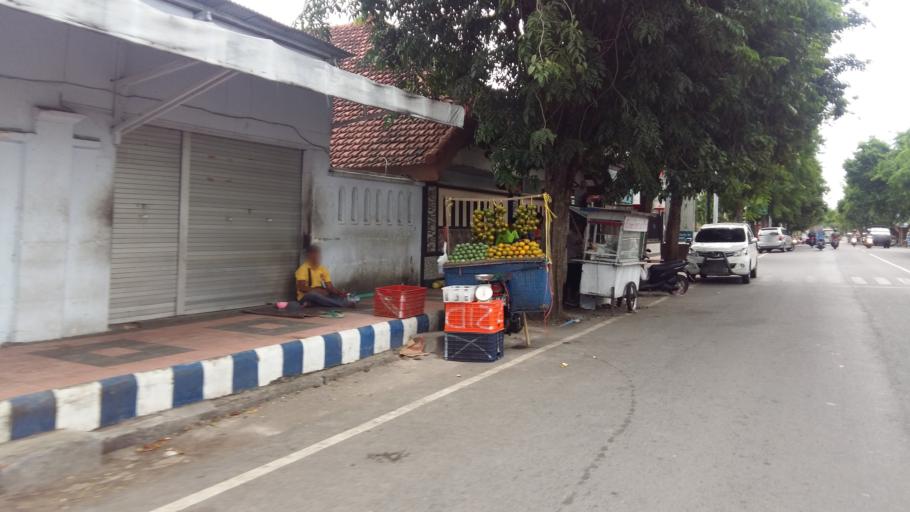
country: ID
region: East Java
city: Krajan
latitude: -8.3092
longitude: 114.2927
